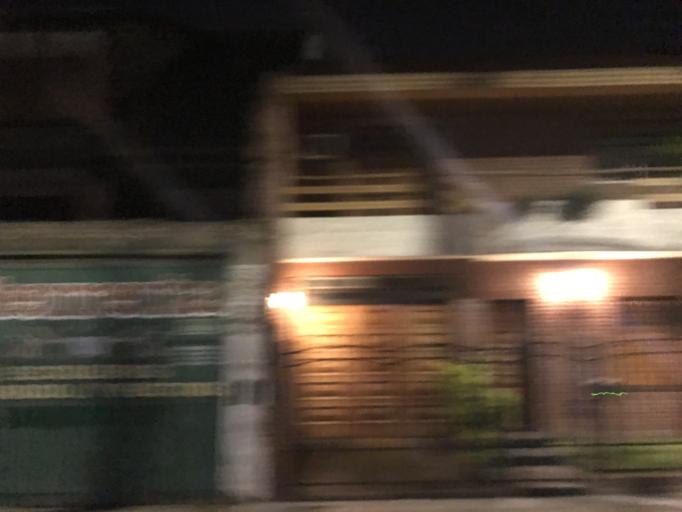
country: AR
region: Buenos Aires
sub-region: Partido de Lanus
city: Lanus
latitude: -34.6742
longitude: -58.4062
